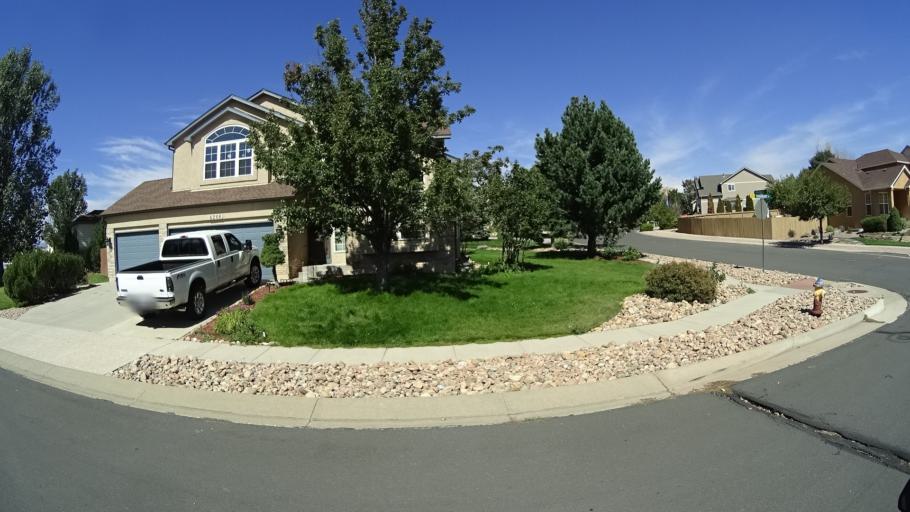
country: US
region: Colorado
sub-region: El Paso County
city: Cimarron Hills
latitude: 38.8944
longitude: -104.7053
